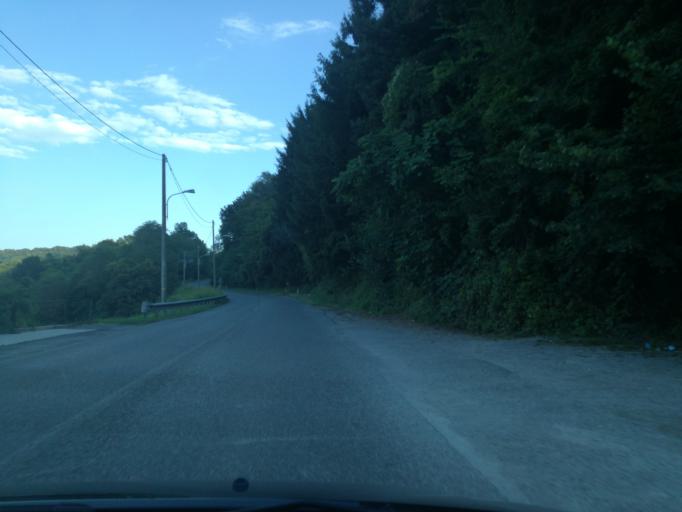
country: IT
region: Lombardy
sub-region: Provincia di Lecco
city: Imbersago
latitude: 45.7145
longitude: 9.4443
